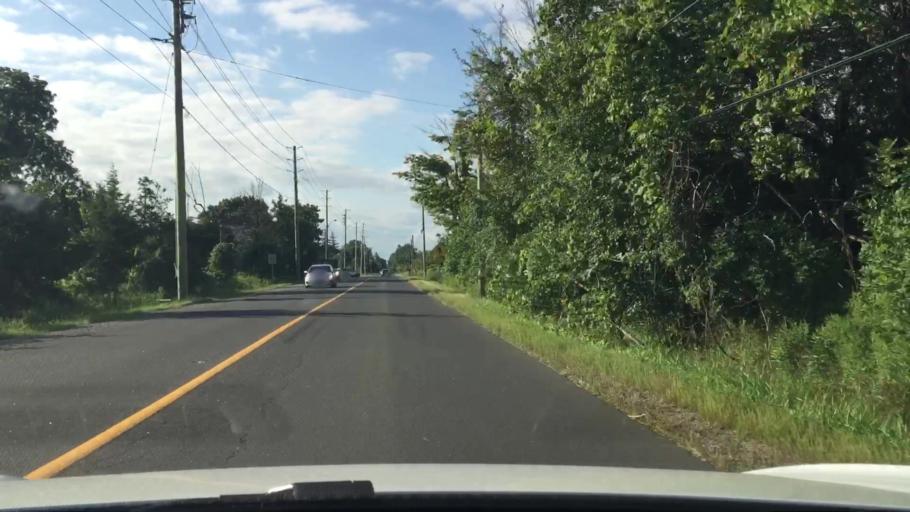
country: CA
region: Ontario
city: Markham
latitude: 43.8674
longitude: -79.2064
